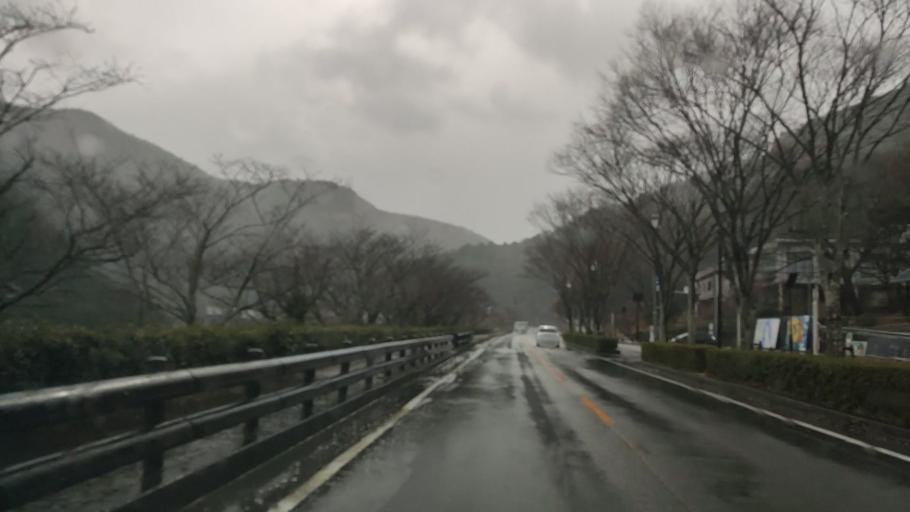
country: JP
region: Tokushima
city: Kamojimacho-jogejima
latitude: 34.1510
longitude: 134.3527
